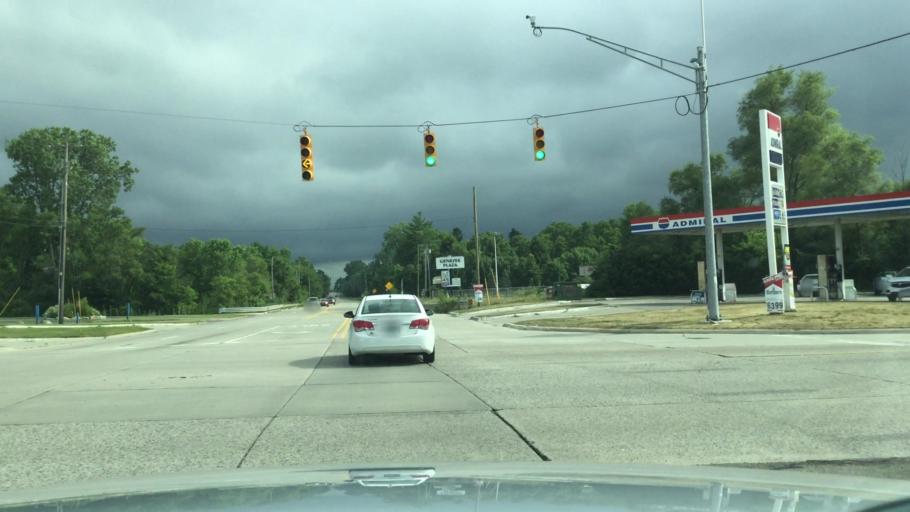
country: US
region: Michigan
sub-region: Genesee County
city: Burton
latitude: 43.0513
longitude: -83.6160
